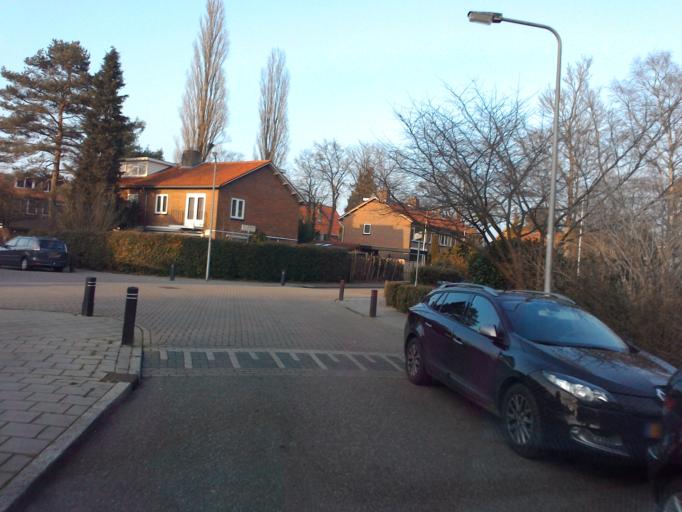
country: NL
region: Utrecht
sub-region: Gemeente Zeist
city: Zeist
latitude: 52.0988
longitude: 5.2514
